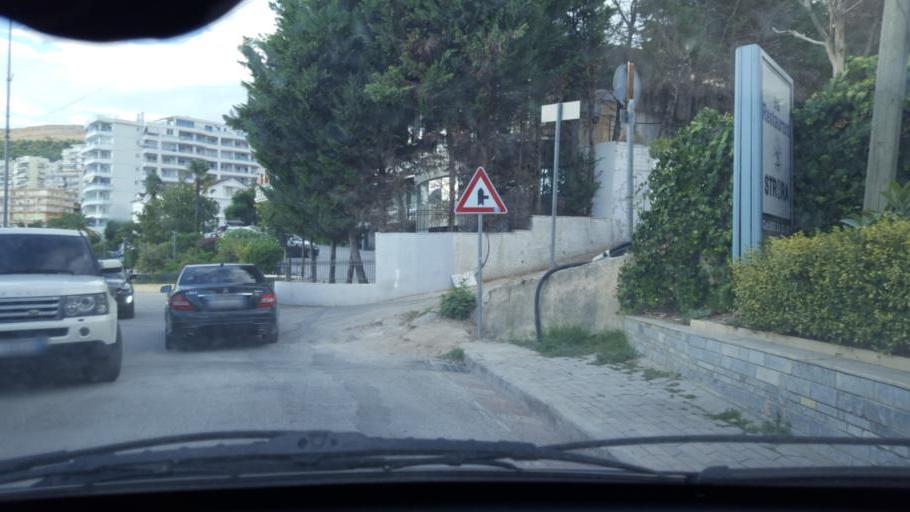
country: AL
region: Vlore
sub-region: Rrethi i Sarandes
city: Sarande
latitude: 39.8703
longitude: 20.0145
